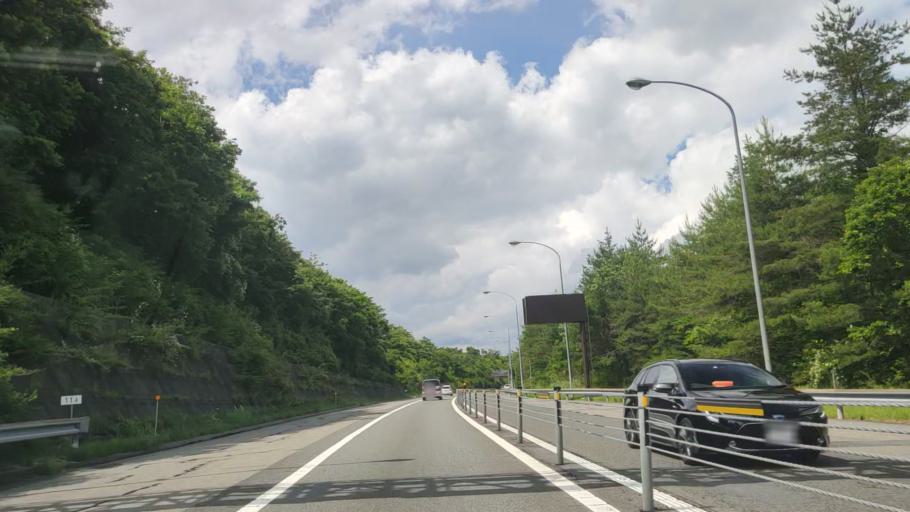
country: JP
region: Shizuoka
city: Gotemba
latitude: 35.4077
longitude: 138.8378
